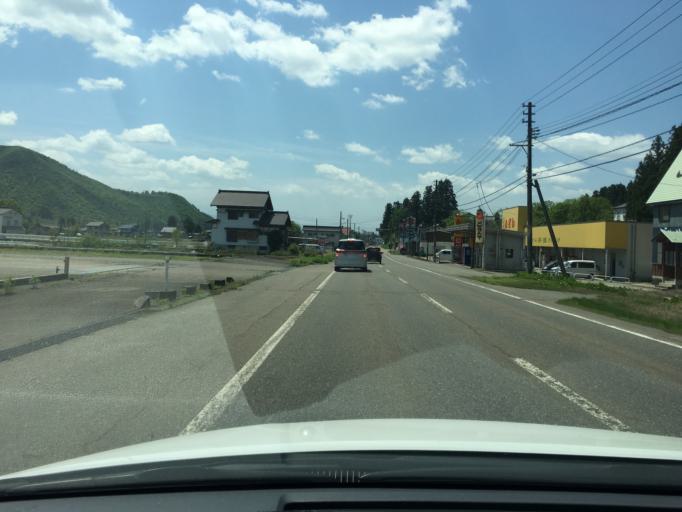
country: JP
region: Niigata
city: Ojiya
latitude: 37.2855
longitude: 138.9872
